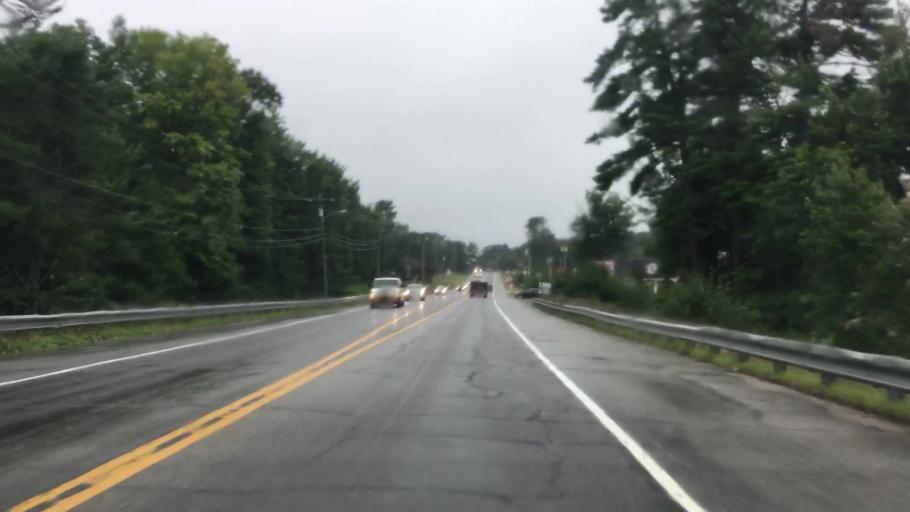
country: US
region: Maine
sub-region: Cumberland County
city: Raymond
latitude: 43.9655
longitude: -70.5794
